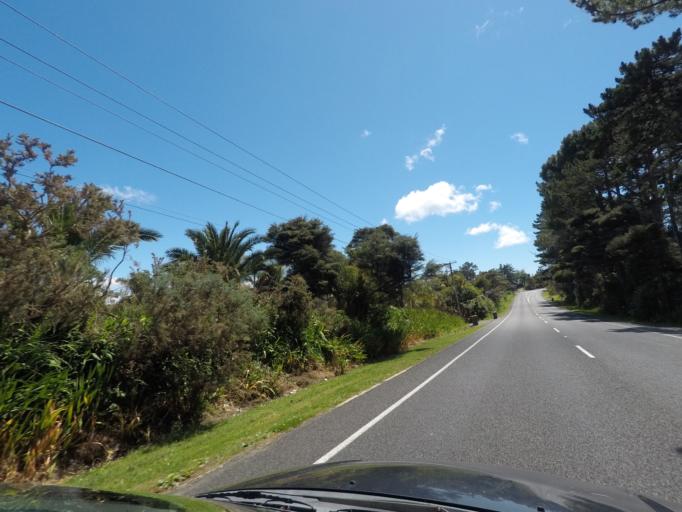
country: NZ
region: Auckland
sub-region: Auckland
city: Rothesay Bay
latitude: -36.7309
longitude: 174.6768
